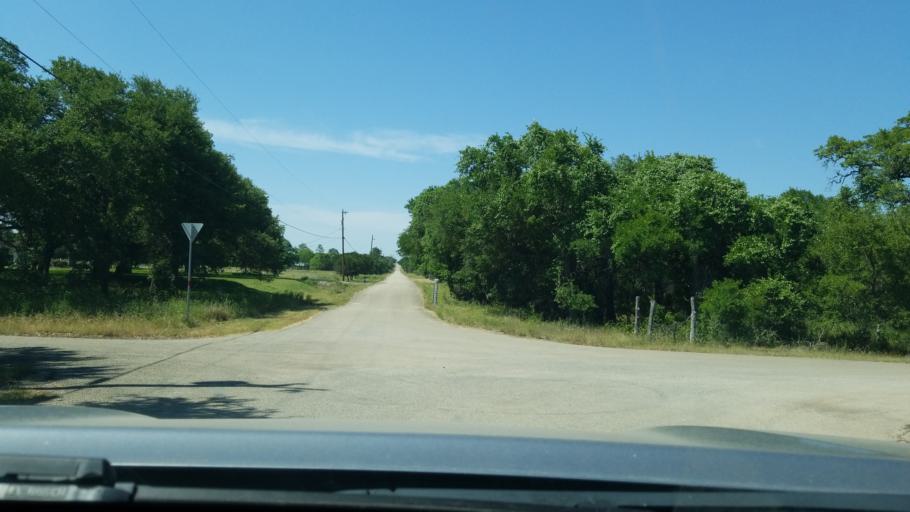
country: US
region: Texas
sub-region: Bexar County
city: Timberwood Park
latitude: 29.7501
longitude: -98.5179
